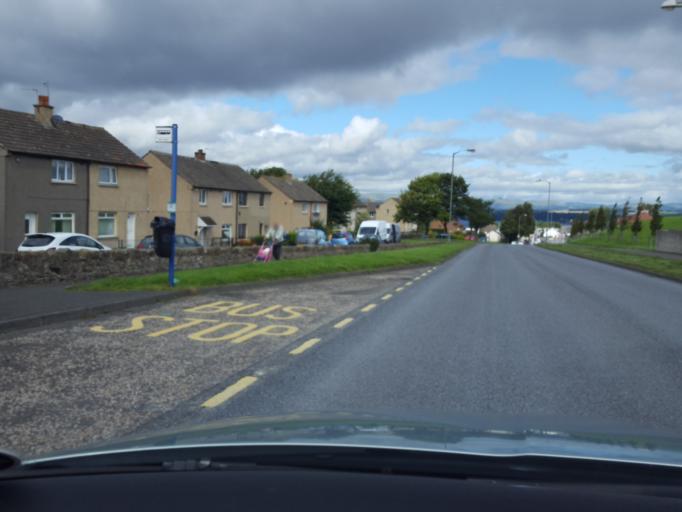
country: GB
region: Scotland
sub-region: Falkirk
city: Bo'ness
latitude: 56.0061
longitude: -3.6099
